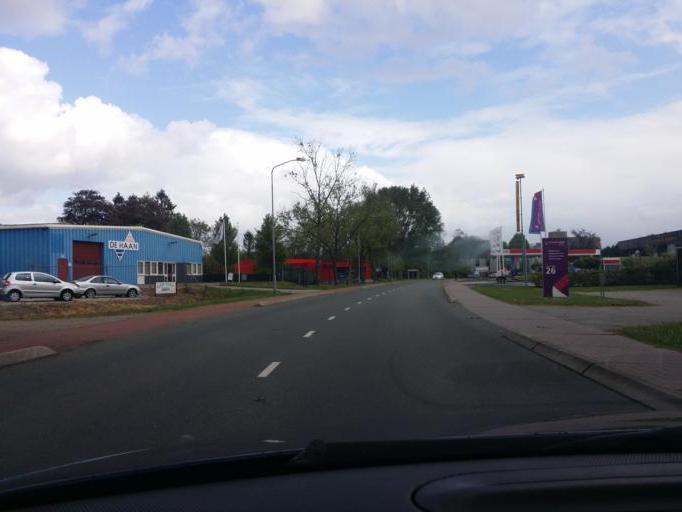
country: NL
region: Groningen
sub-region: Gemeente Hoogezand-Sappemeer
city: Hoogezand
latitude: 53.1654
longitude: 6.7375
